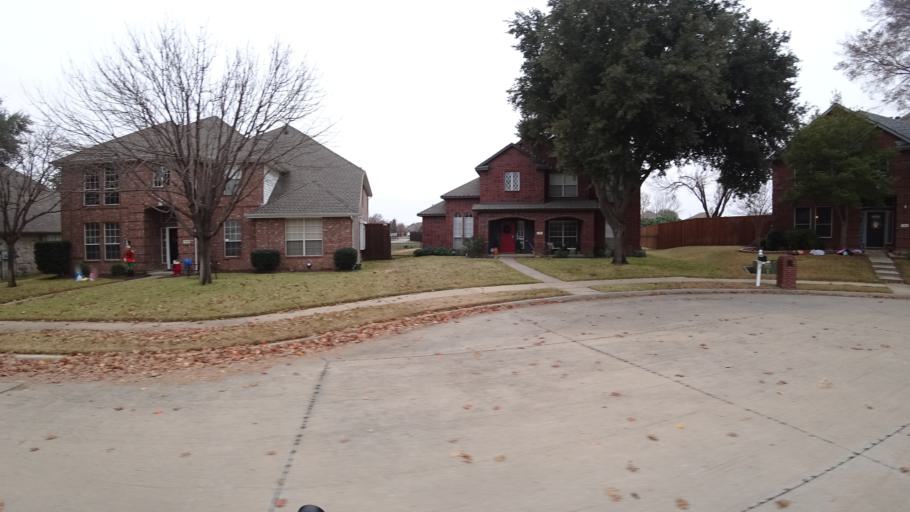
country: US
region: Texas
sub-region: Denton County
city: Highland Village
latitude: 33.0587
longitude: -97.0302
